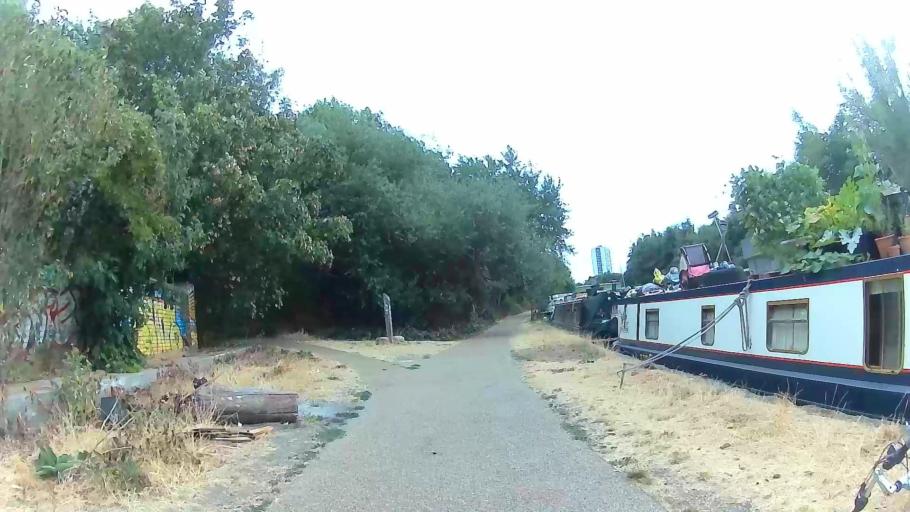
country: GB
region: England
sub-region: Greater London
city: Hackney
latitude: 51.5598
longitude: -0.0397
